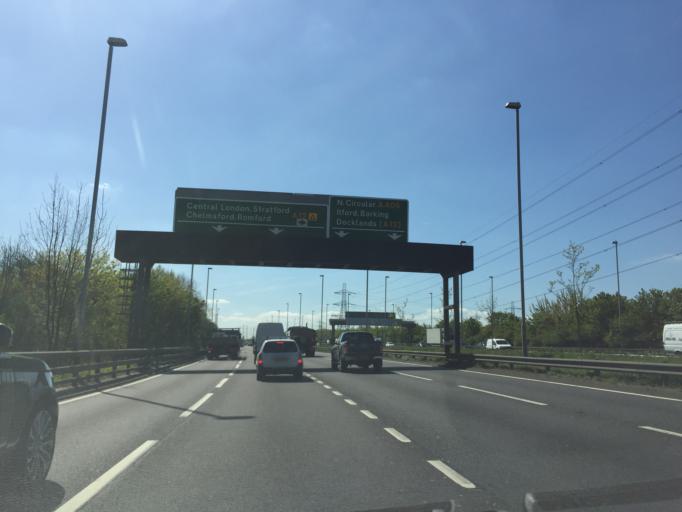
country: GB
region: England
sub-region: Greater London
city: Woodford Green
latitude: 51.5818
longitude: 0.0408
